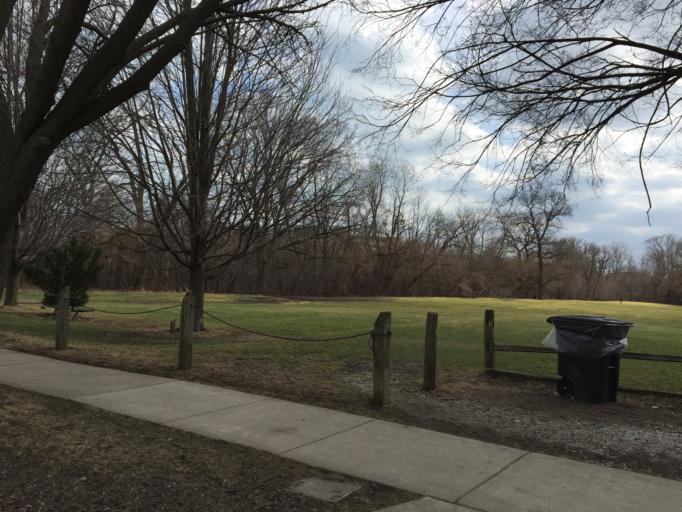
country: US
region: Illinois
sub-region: Cook County
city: Evanston
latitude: 42.0688
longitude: -87.6875
